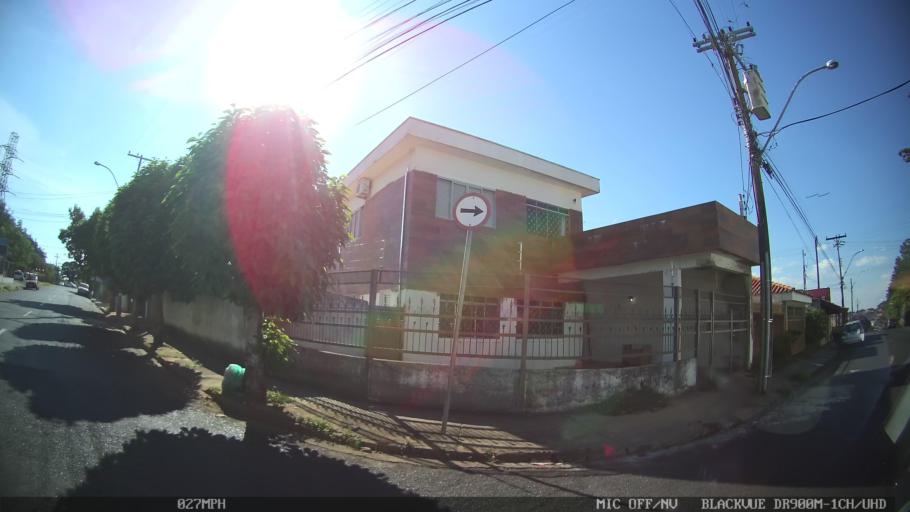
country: BR
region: Sao Paulo
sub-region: Ribeirao Preto
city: Ribeirao Preto
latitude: -21.1866
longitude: -47.7827
